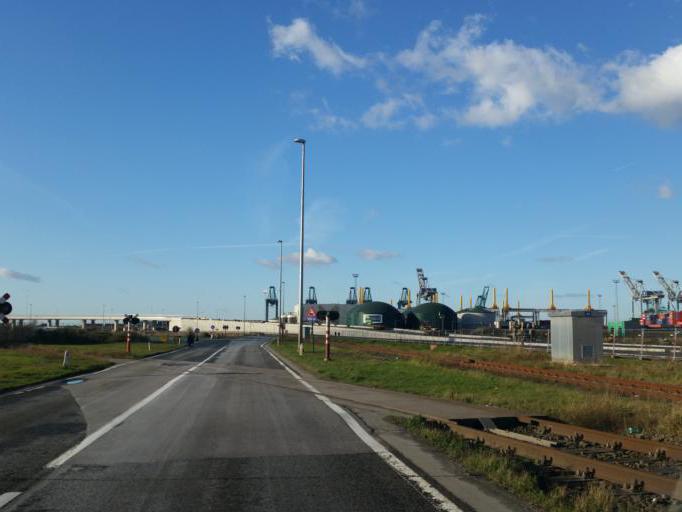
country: BE
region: Flanders
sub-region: Provincie Oost-Vlaanderen
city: Beveren
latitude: 51.2812
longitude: 4.2716
